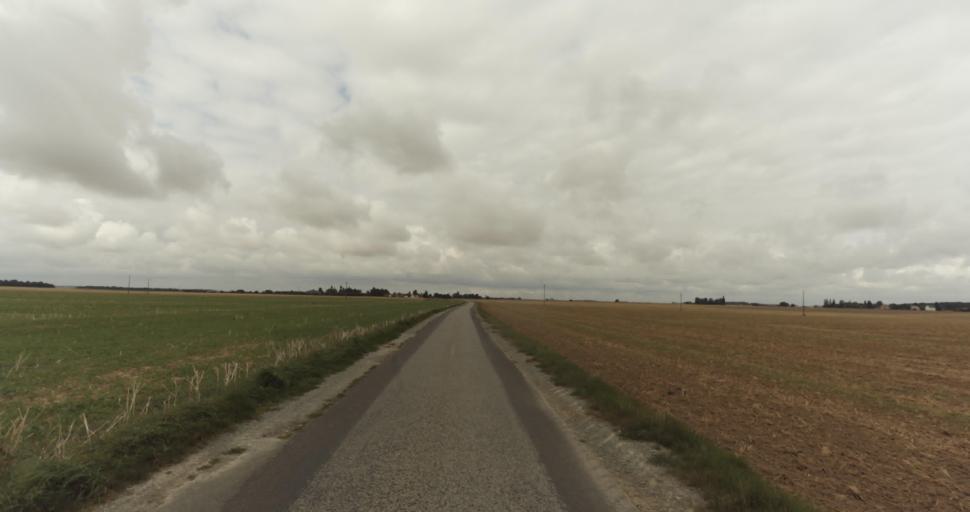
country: FR
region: Haute-Normandie
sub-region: Departement de l'Eure
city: La Couture-Boussey
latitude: 48.9359
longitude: 1.3802
